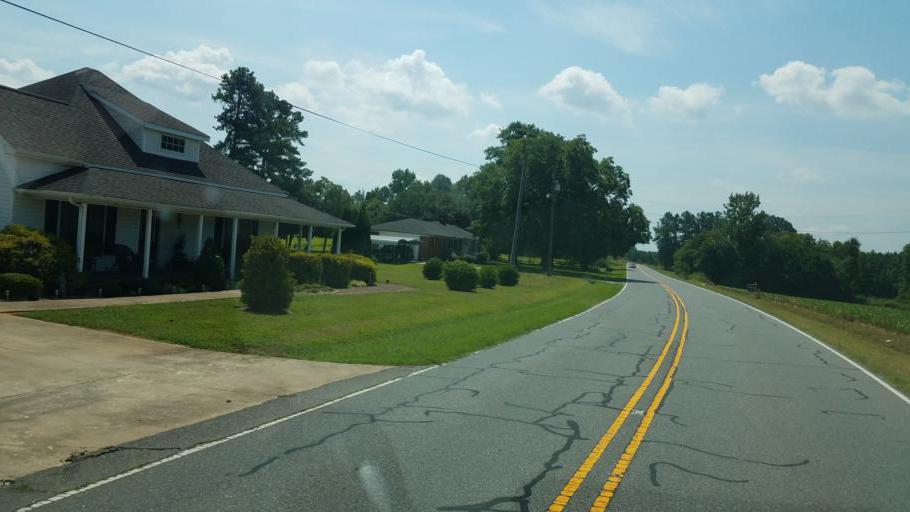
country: US
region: North Carolina
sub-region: Gaston County
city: Cherryville
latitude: 35.4579
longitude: -81.4335
